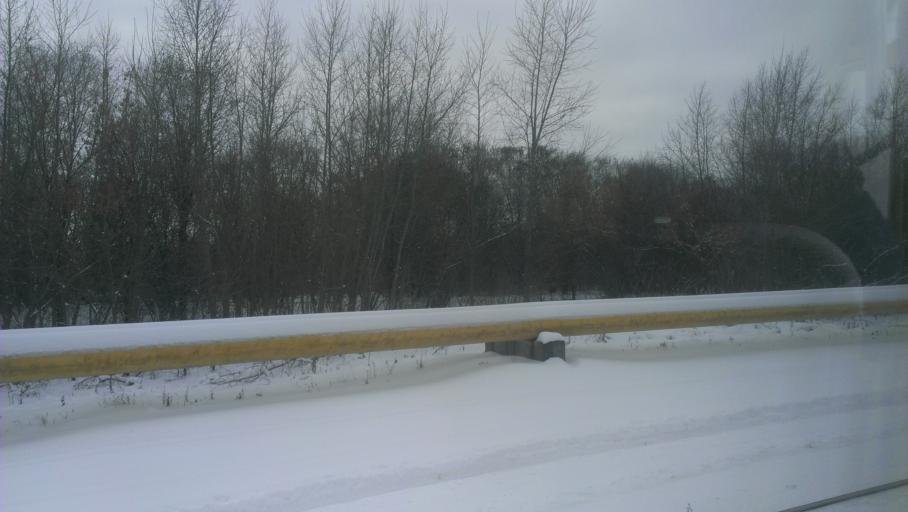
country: RU
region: Altai Krai
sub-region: Gorod Barnaulskiy
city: Barnaul
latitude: 53.3872
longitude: 83.7011
